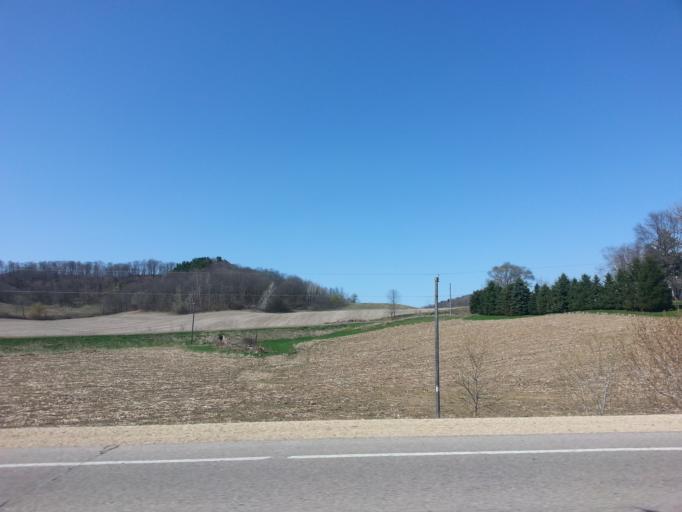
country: US
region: Wisconsin
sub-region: Dunn County
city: Menomonie
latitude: 44.8953
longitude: -92.0262
